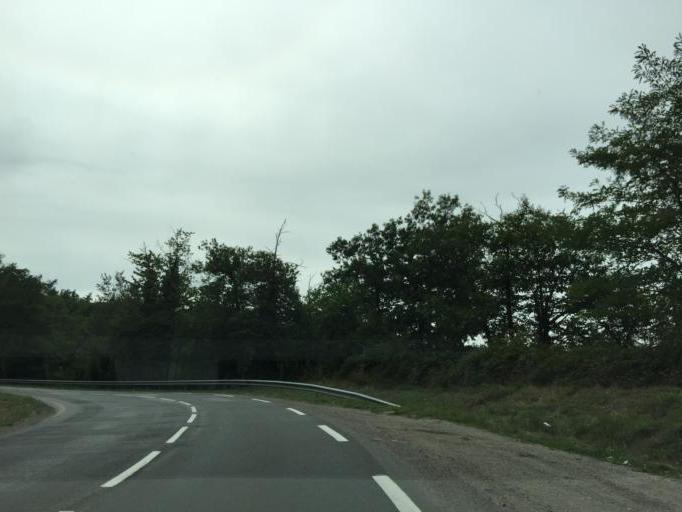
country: FR
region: Midi-Pyrenees
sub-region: Departement de l'Aveyron
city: Villefranche-de-Rouergue
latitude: 44.3187
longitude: 2.0303
